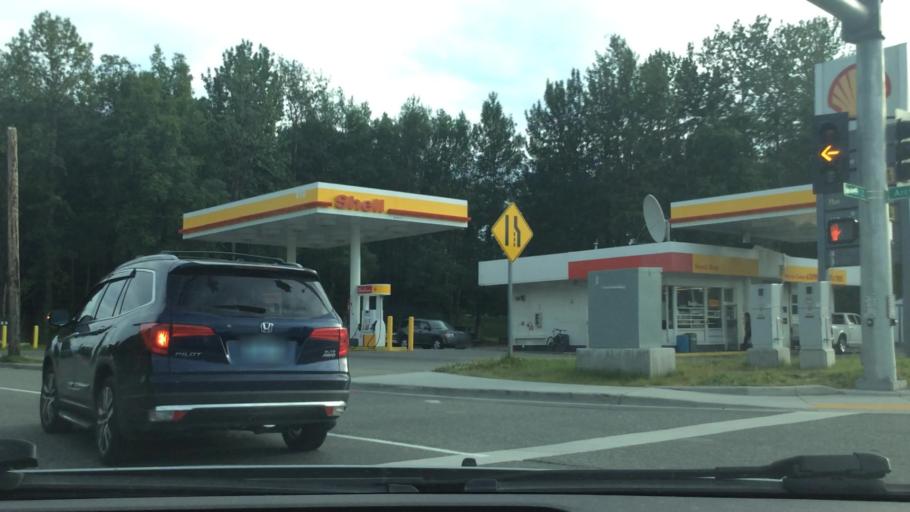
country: US
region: Alaska
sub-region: Anchorage Municipality
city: Anchorage
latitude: 61.1807
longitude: -149.8980
